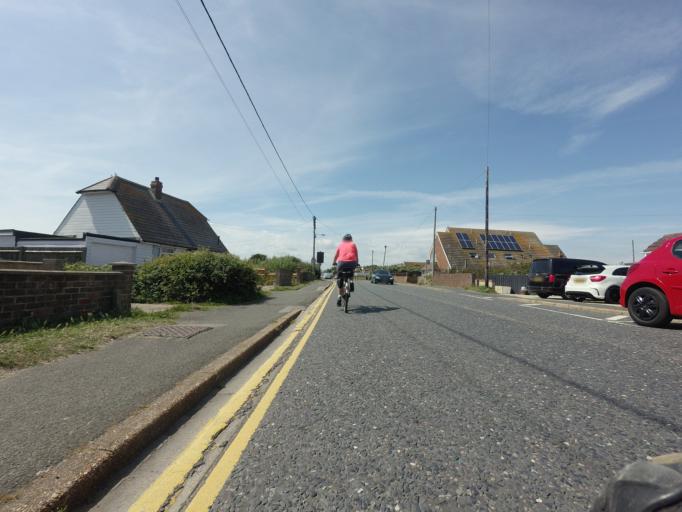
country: GB
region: England
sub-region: East Sussex
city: Rye
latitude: 50.9334
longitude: 0.8019
